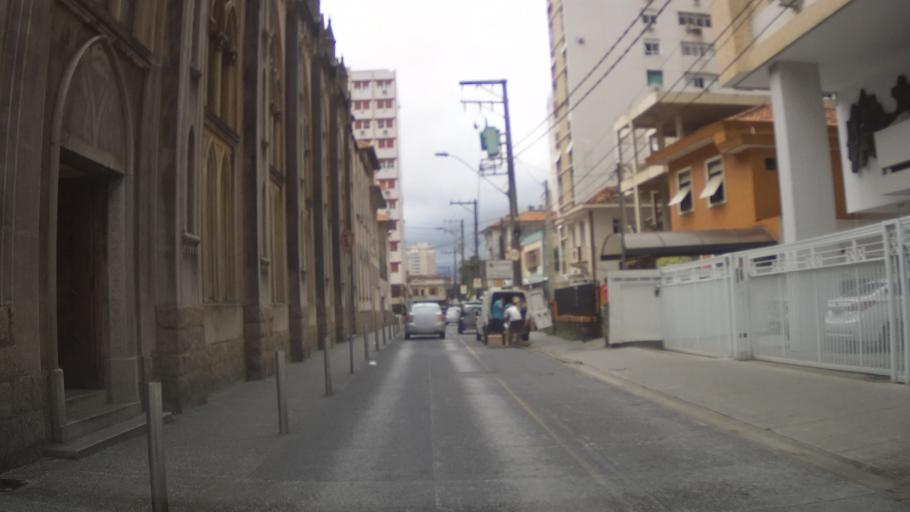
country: BR
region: Sao Paulo
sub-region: Santos
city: Santos
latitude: -23.9744
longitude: -46.3200
